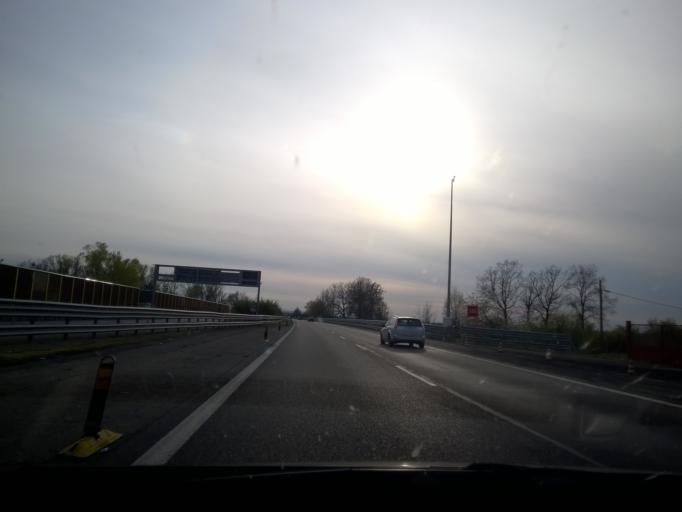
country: IT
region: Emilia-Romagna
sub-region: Provincia di Piacenza
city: Caorso
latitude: 45.0517
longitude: 9.8644
